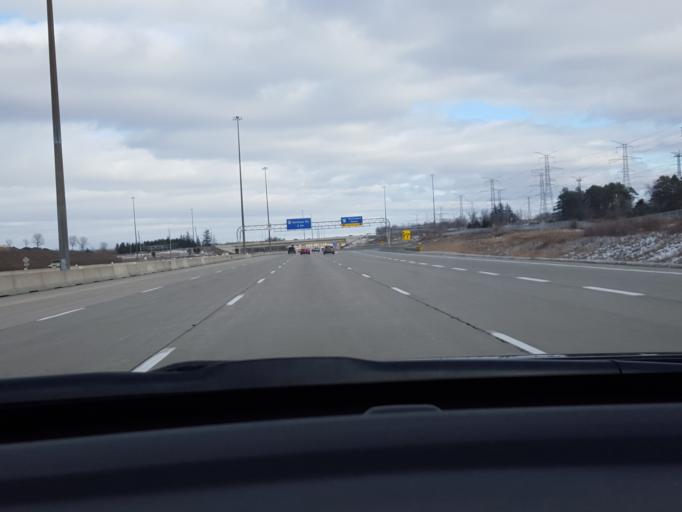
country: CA
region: Ontario
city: Markham
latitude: 43.8543
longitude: -79.2894
